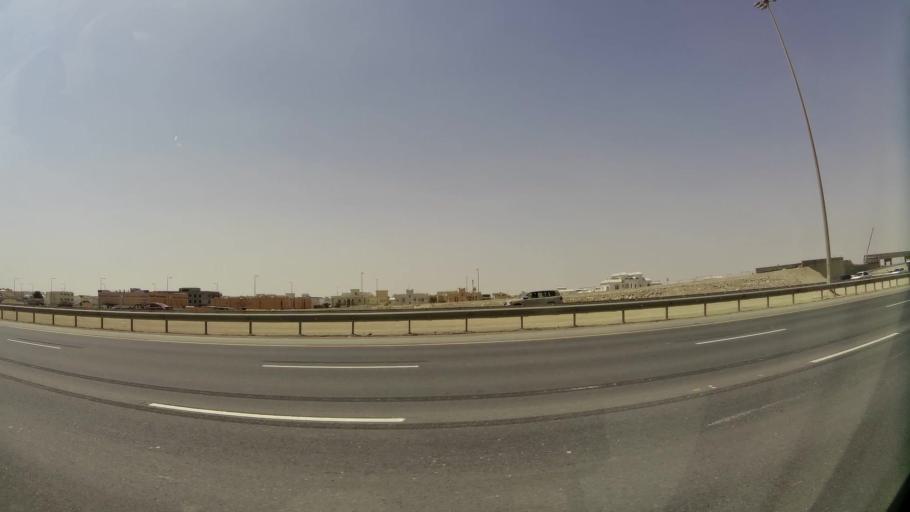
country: QA
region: Baladiyat Umm Salal
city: Umm Salal Muhammad
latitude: 25.3981
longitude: 51.4313
